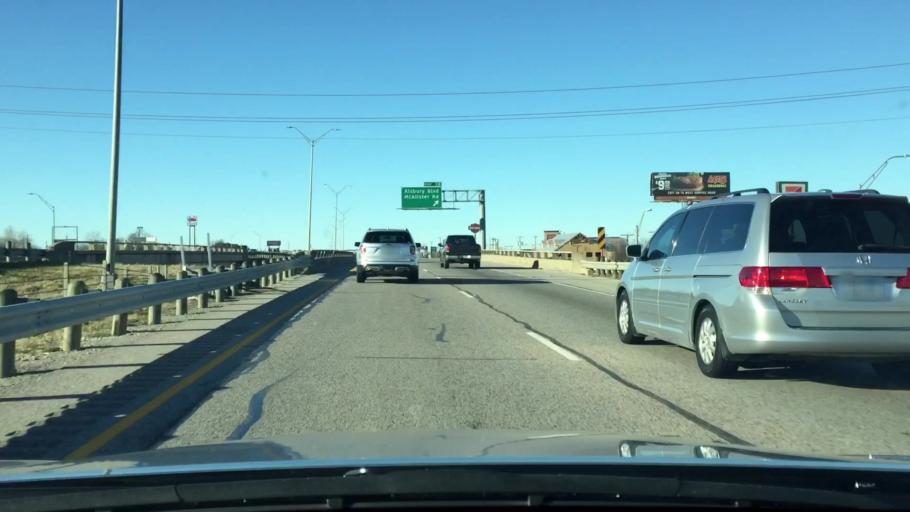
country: US
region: Texas
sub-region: Johnson County
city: Burleson
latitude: 32.5434
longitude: -97.3145
